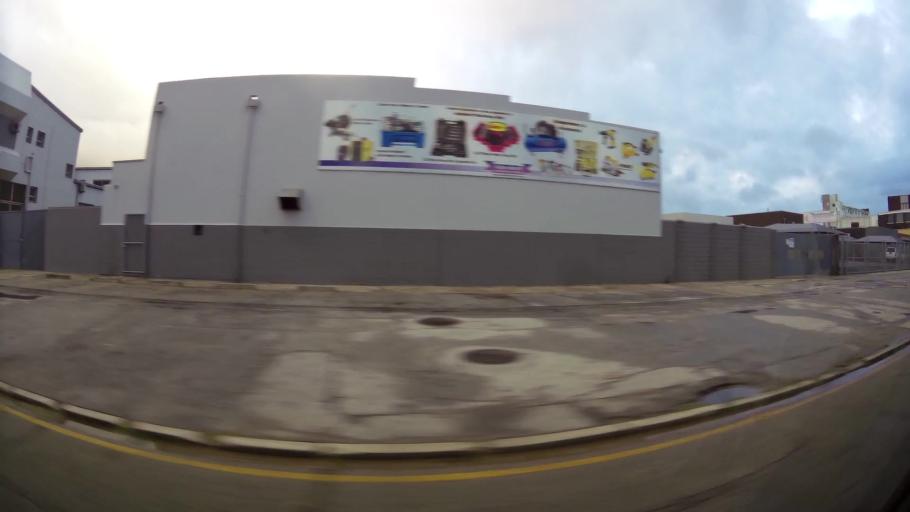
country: ZA
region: Eastern Cape
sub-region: Nelson Mandela Bay Metropolitan Municipality
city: Port Elizabeth
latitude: -33.9345
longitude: 25.6046
